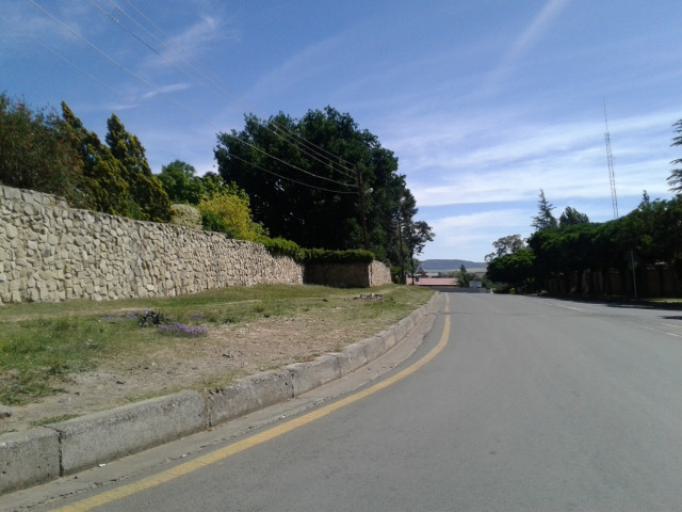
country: LS
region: Maseru
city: Maseru
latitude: -29.3086
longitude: 27.4788
